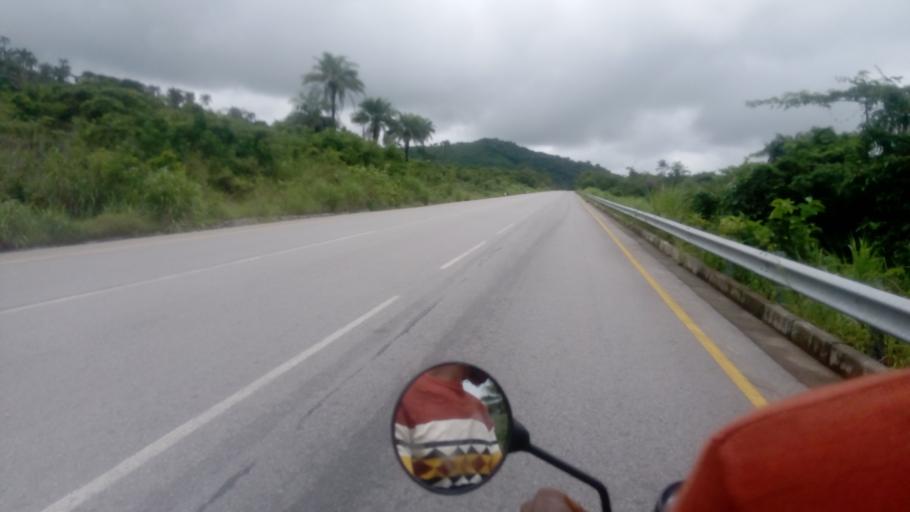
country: SL
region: Northern Province
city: Masaka
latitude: 8.6616
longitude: -11.7902
